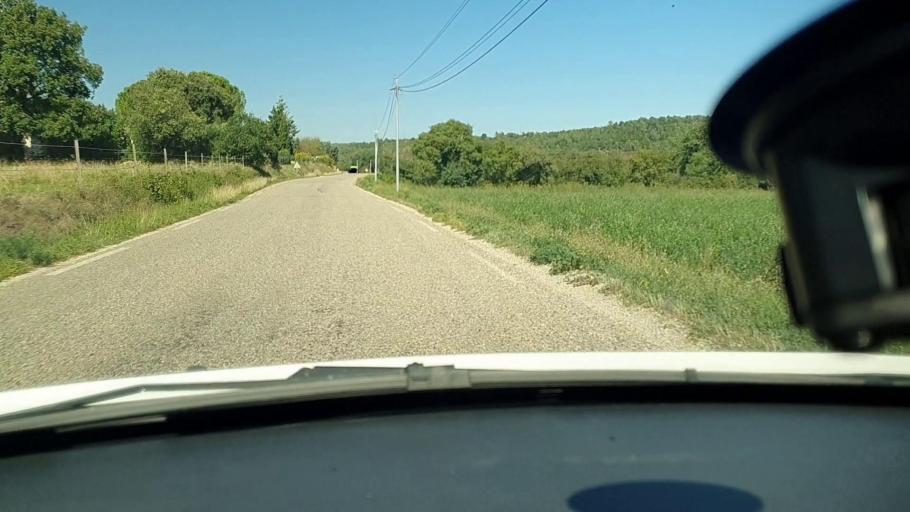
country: FR
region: Languedoc-Roussillon
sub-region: Departement du Gard
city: Goudargues
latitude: 44.1577
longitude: 4.4588
